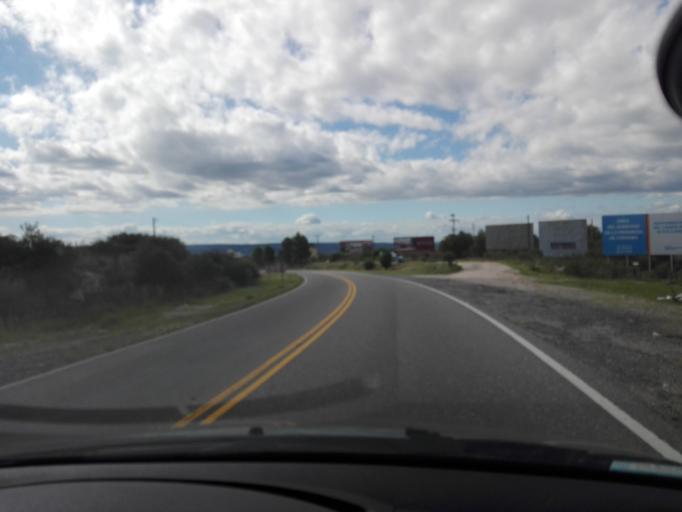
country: AR
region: Cordoba
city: Mina Clavero
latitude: -31.7501
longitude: -64.9784
